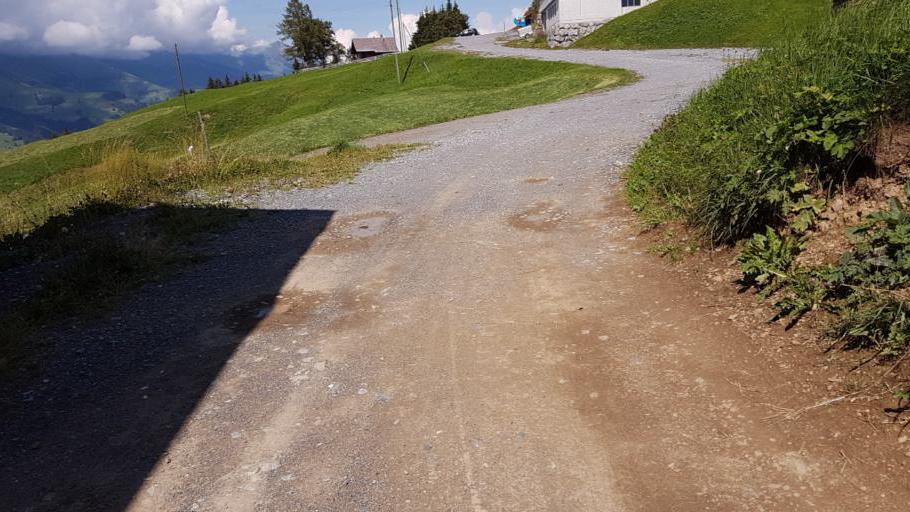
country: CH
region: Bern
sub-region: Frutigen-Niedersimmental District
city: Adelboden
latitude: 46.5156
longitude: 7.6020
